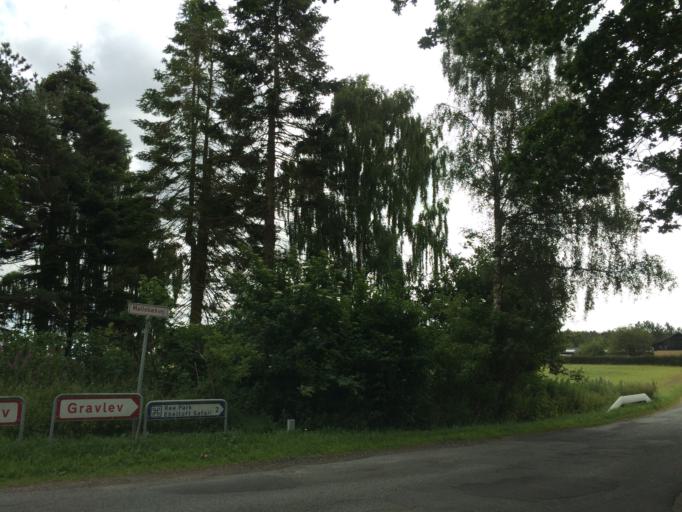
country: DK
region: Central Jutland
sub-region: Syddjurs Kommune
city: Ebeltoft
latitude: 56.2740
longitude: 10.7264
